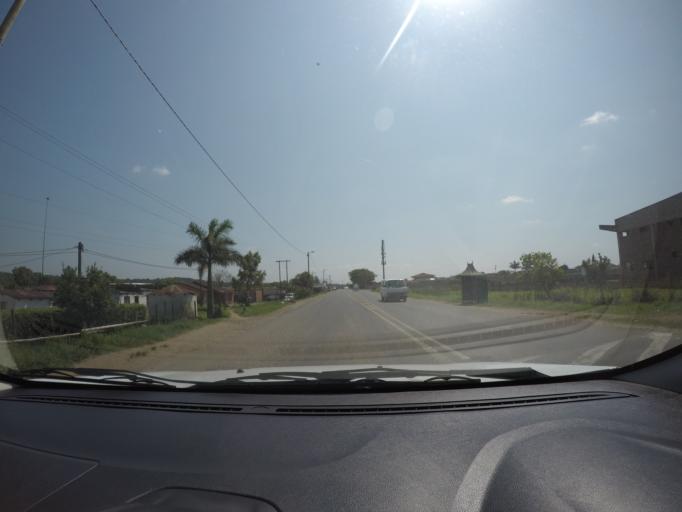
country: ZA
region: KwaZulu-Natal
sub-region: uThungulu District Municipality
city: eSikhawini
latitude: -28.8654
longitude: 31.9090
